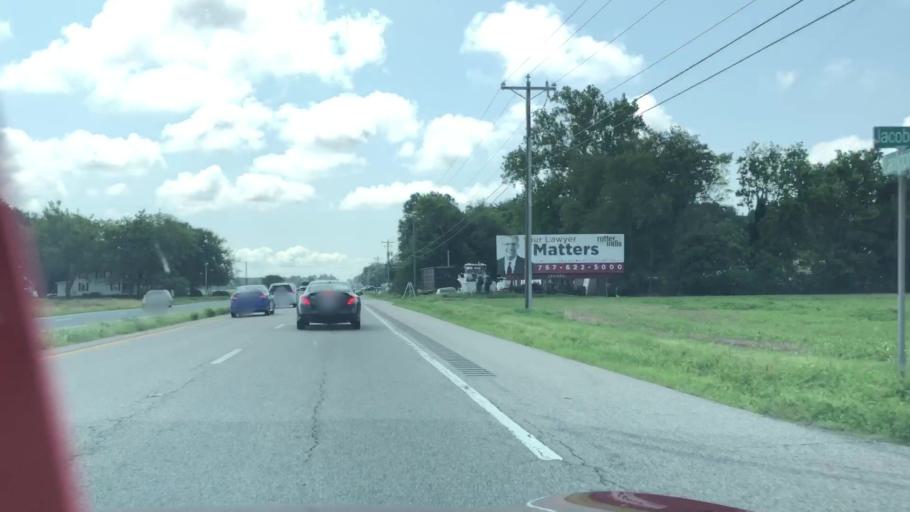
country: US
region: Virginia
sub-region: Northampton County
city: Cape Charles
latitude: 37.2492
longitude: -75.9724
